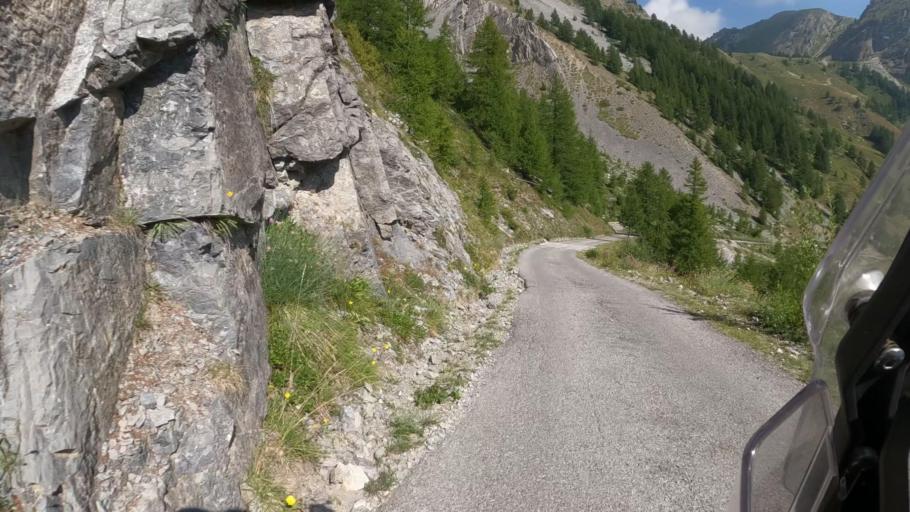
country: IT
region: Piedmont
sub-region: Provincia di Cuneo
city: Canosio
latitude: 44.4096
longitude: 7.0359
